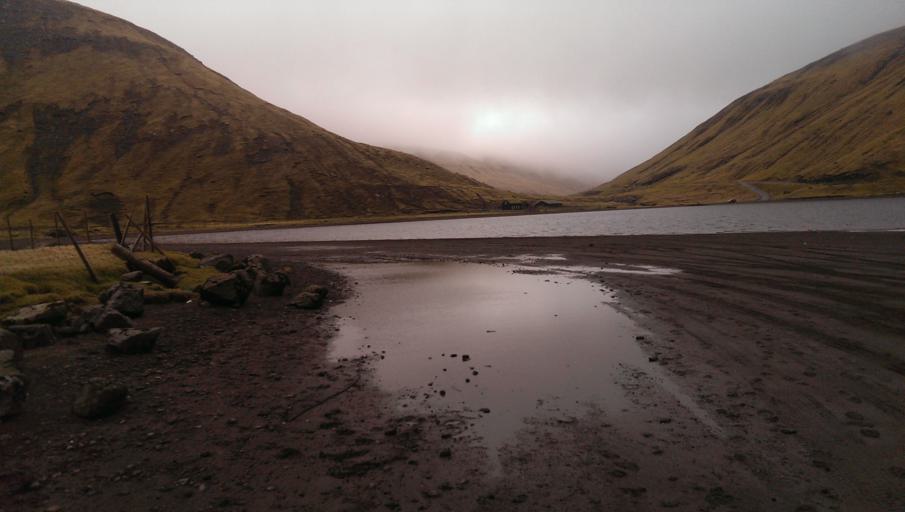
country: FO
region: Streymoy
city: Kollafjordhur
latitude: 62.1306
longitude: -7.0233
